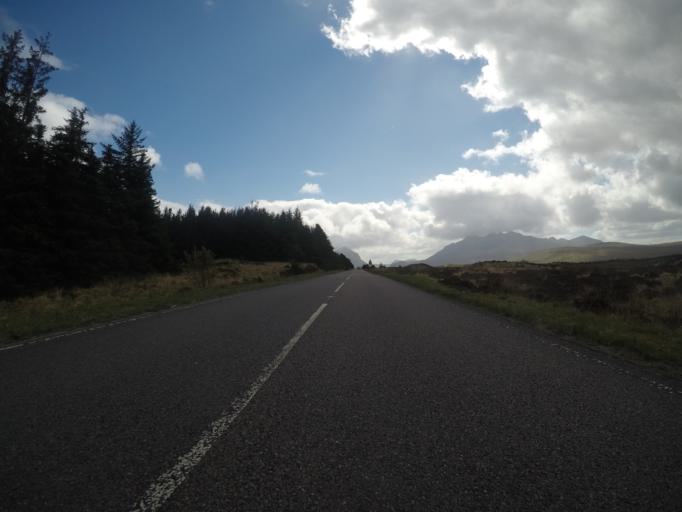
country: GB
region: Scotland
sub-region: Highland
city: Isle of Skye
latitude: 57.3190
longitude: -6.2035
